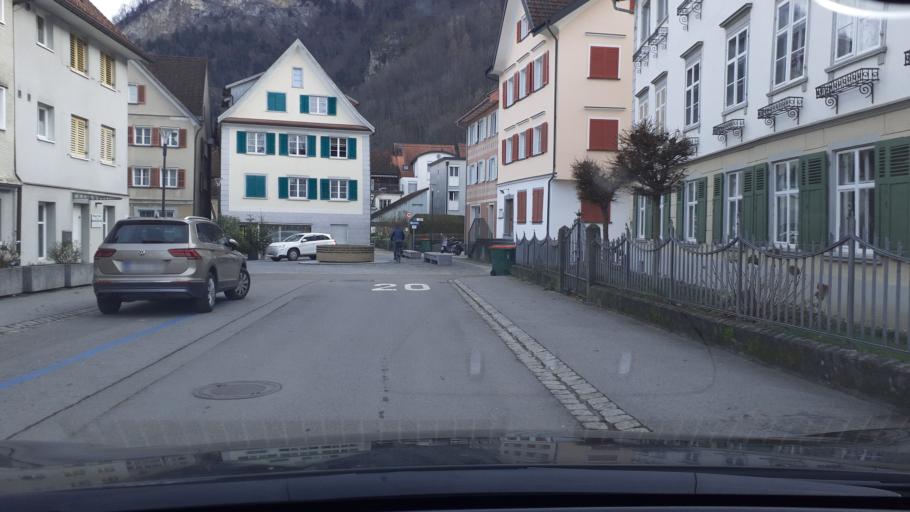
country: AT
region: Vorarlberg
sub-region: Politischer Bezirk Dornbirn
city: Hohenems
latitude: 47.3648
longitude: 9.6878
